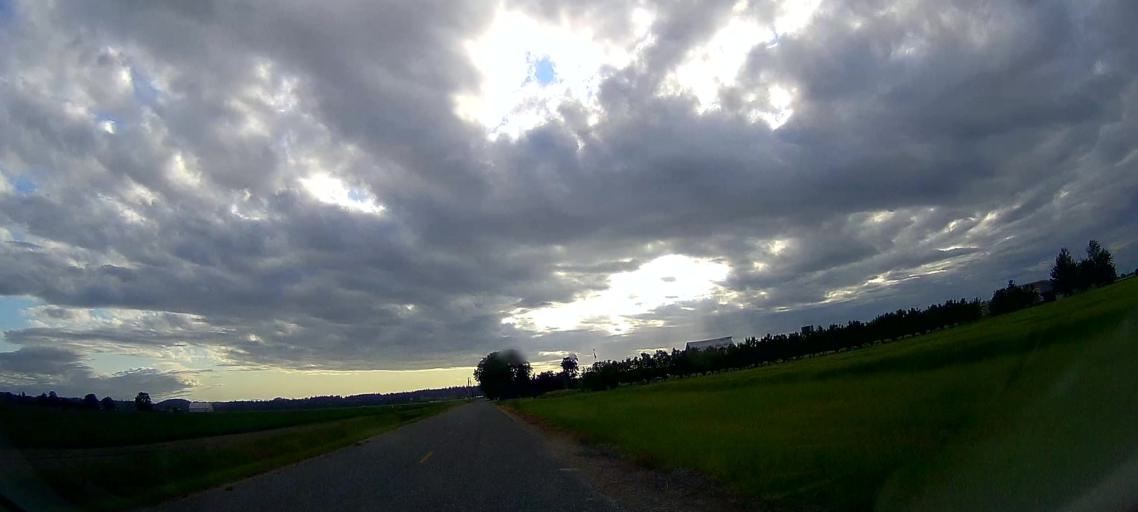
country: US
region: Washington
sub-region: Skagit County
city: Mount Vernon
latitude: 48.3849
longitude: -122.3913
